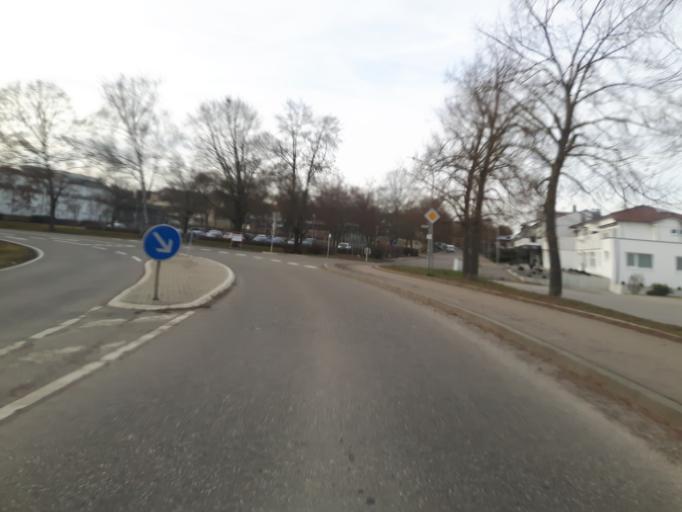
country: DE
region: Baden-Wuerttemberg
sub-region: Regierungsbezirk Stuttgart
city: Bretzfeld
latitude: 49.1784
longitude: 9.4384
